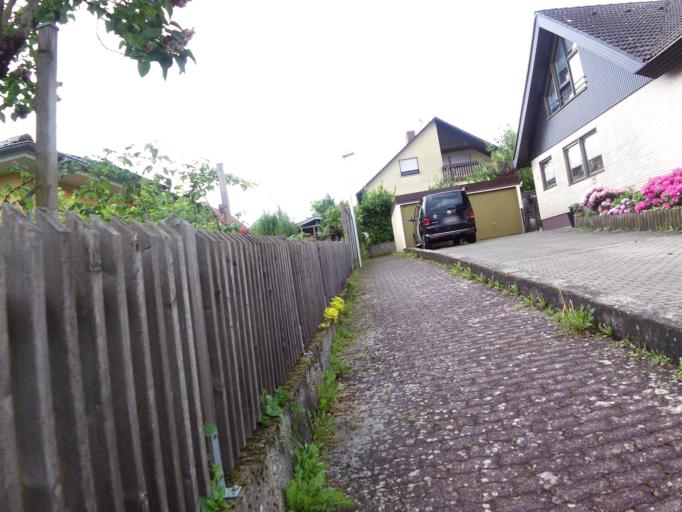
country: DE
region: Bavaria
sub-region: Regierungsbezirk Unterfranken
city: Waldbuttelbrunn
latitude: 49.7865
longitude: 9.8299
